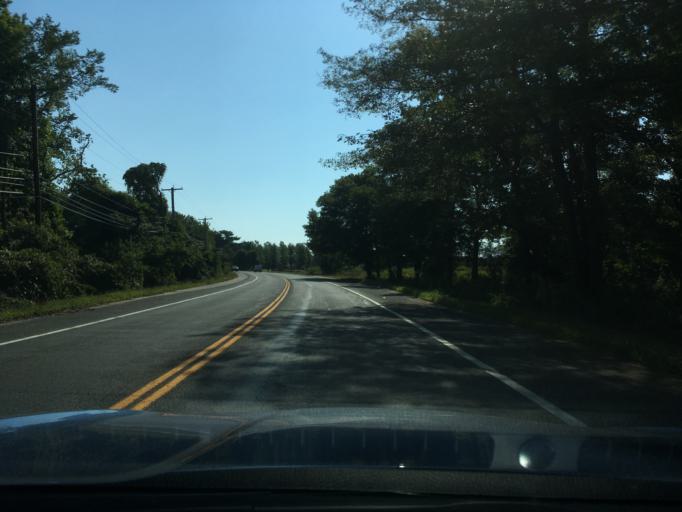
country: US
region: Rhode Island
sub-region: Washington County
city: Exeter
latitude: 41.5761
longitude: -71.5272
